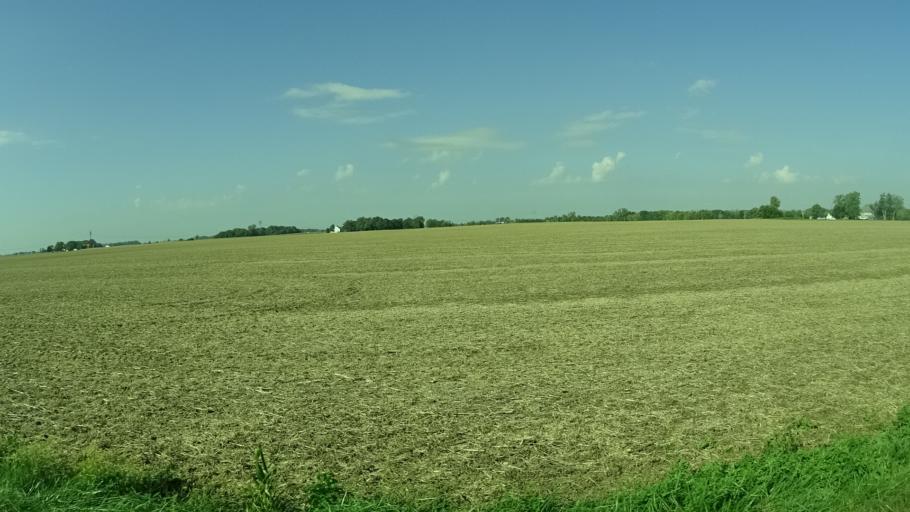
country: US
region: Indiana
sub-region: Madison County
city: Lapel
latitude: 40.0568
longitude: -85.8535
